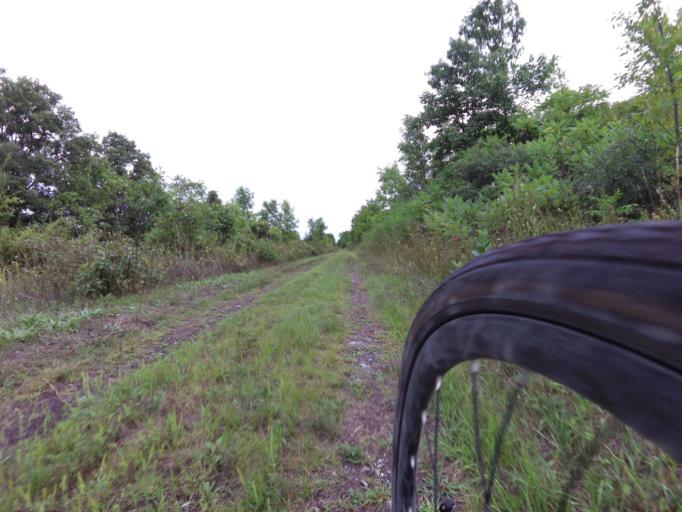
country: CA
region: Ontario
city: Perth
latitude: 44.6261
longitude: -76.2435
